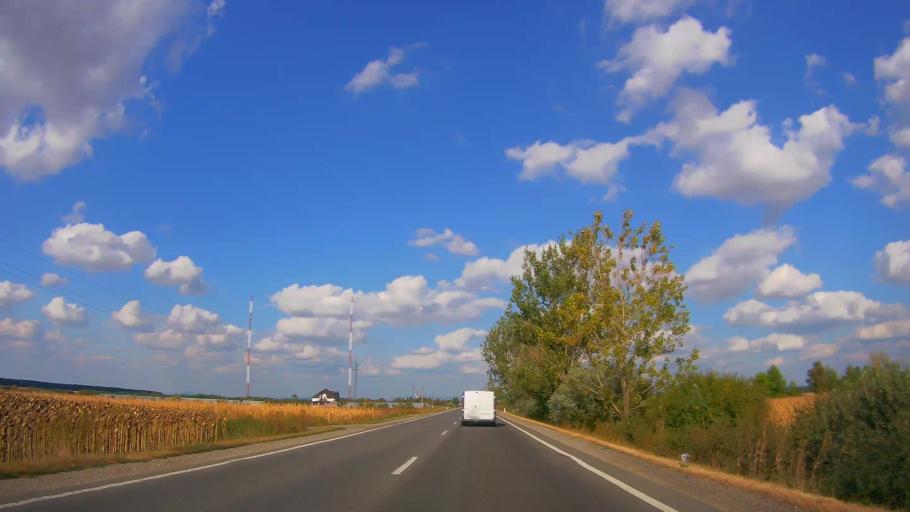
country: RO
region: Satu Mare
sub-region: Comuna Botiz
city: Botiz
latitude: 47.8490
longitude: 22.9704
